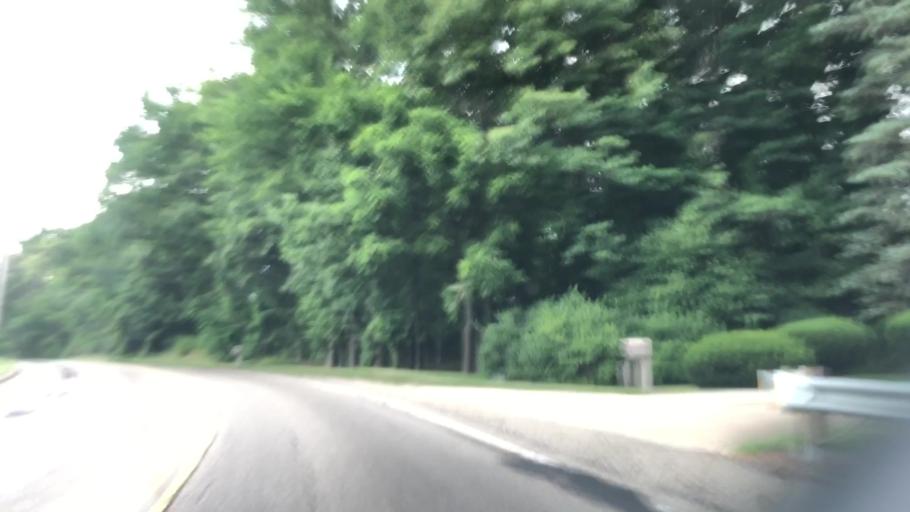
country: US
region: Ohio
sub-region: Summit County
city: New Franklin
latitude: 40.9645
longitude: -81.5217
